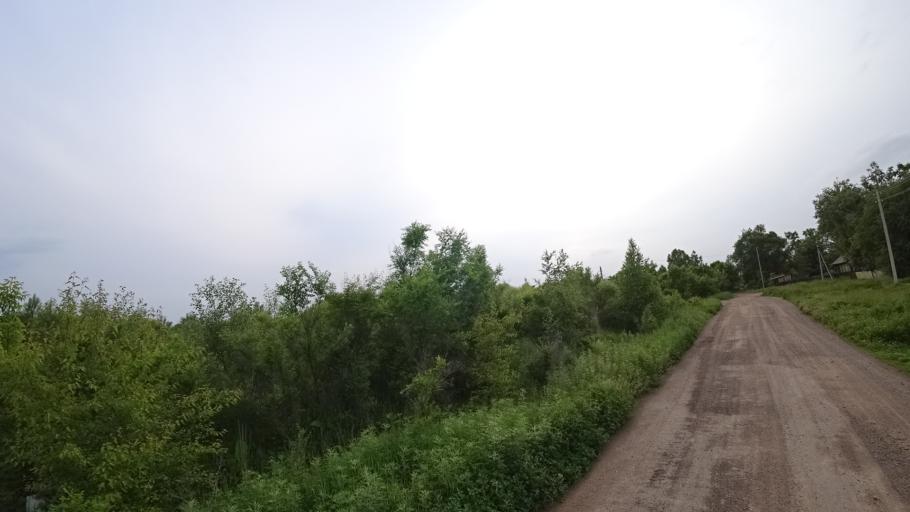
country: RU
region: Primorskiy
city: Novosysoyevka
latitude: 44.2437
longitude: 133.3611
